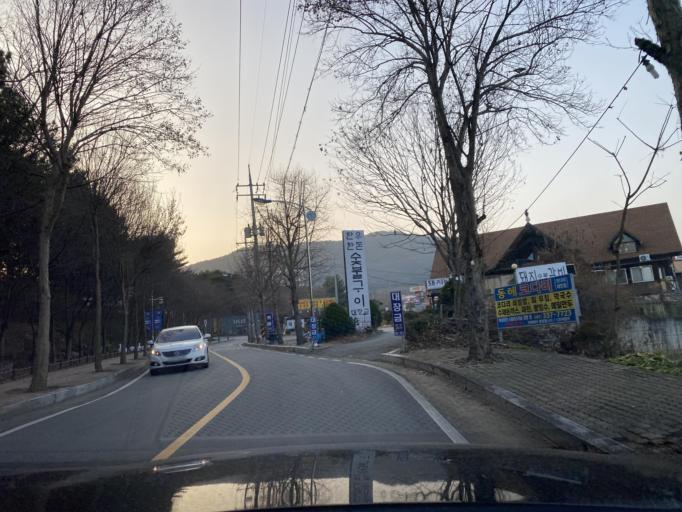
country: KR
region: Chungcheongnam-do
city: Hongsung
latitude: 36.6947
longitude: 126.6577
